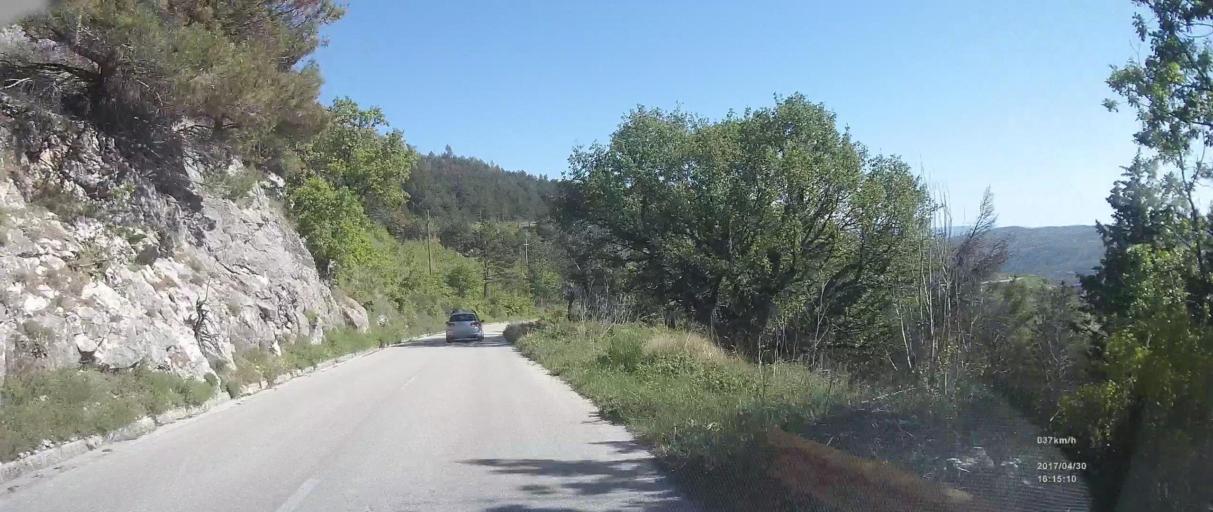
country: HR
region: Splitsko-Dalmatinska
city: Srinjine
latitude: 43.5095
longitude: 16.6056
